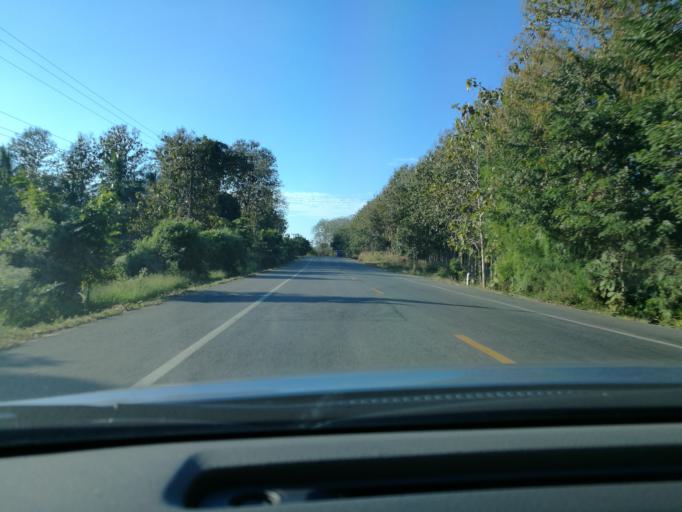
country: TH
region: Phitsanulok
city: Nakhon Thai
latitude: 17.0727
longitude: 100.8348
